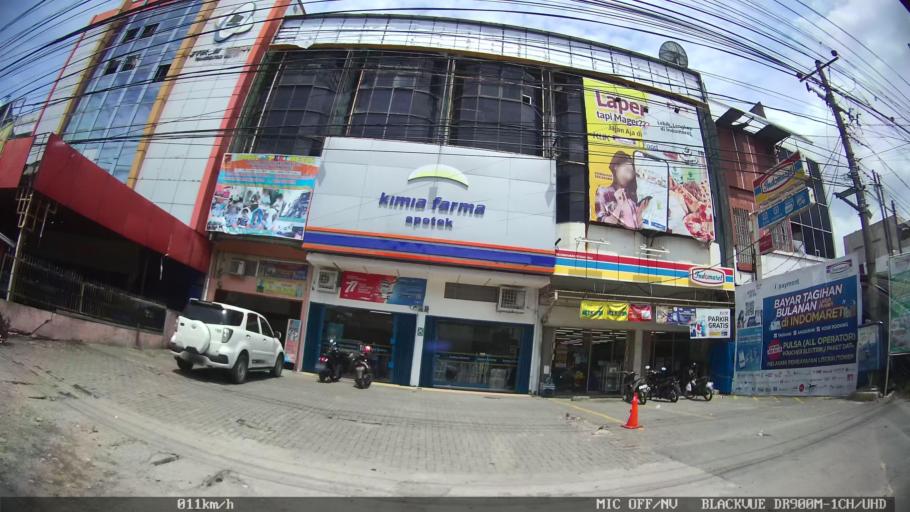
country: ID
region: North Sumatra
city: Medan
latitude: 3.5813
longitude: 98.6613
